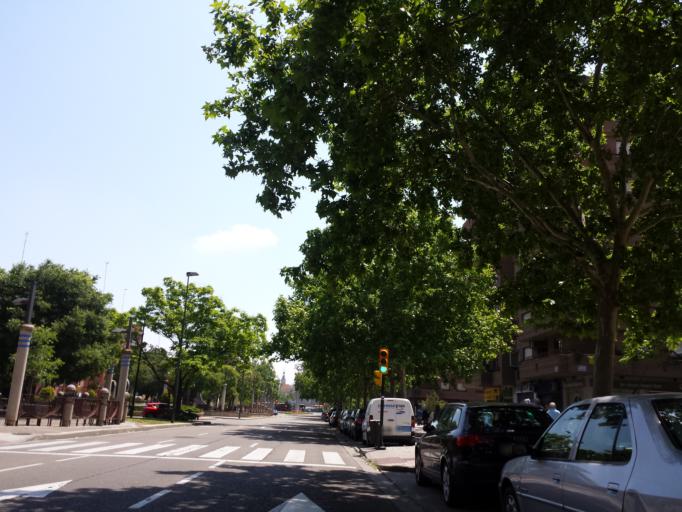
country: ES
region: Aragon
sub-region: Provincia de Zaragoza
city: Almozara
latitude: 41.6600
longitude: -0.8957
